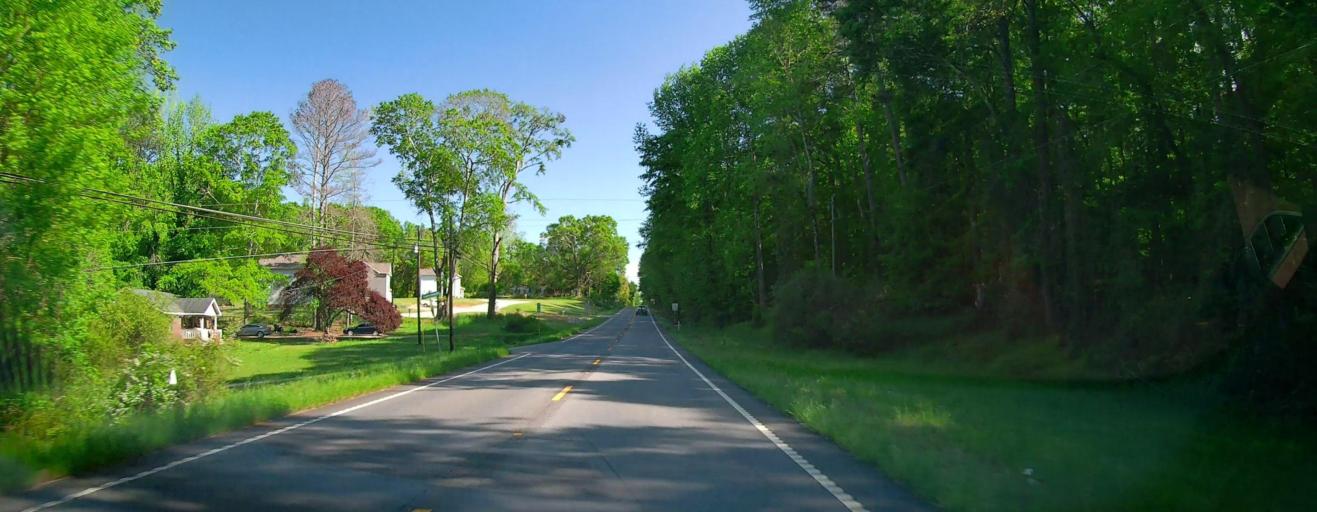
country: US
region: Georgia
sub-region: Morgan County
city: Madison
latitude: 33.6104
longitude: -83.4787
